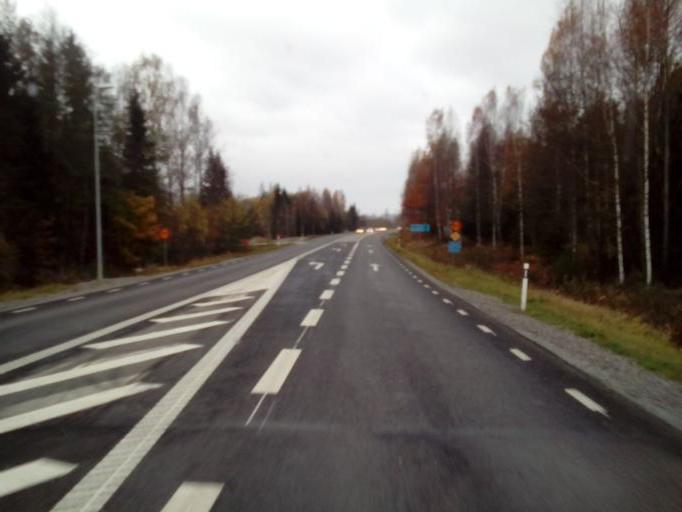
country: SE
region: OErebro
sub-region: Karlskoga Kommun
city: Karlskoga
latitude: 59.2948
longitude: 14.4864
